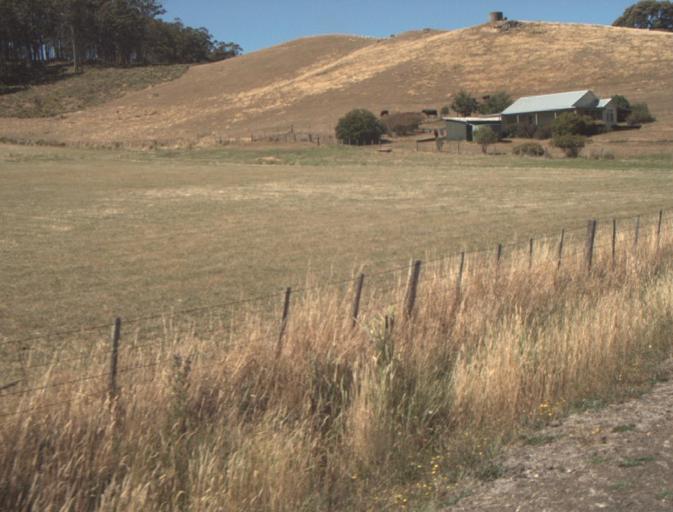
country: AU
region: Tasmania
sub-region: Launceston
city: Newstead
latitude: -41.3430
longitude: 147.3035
